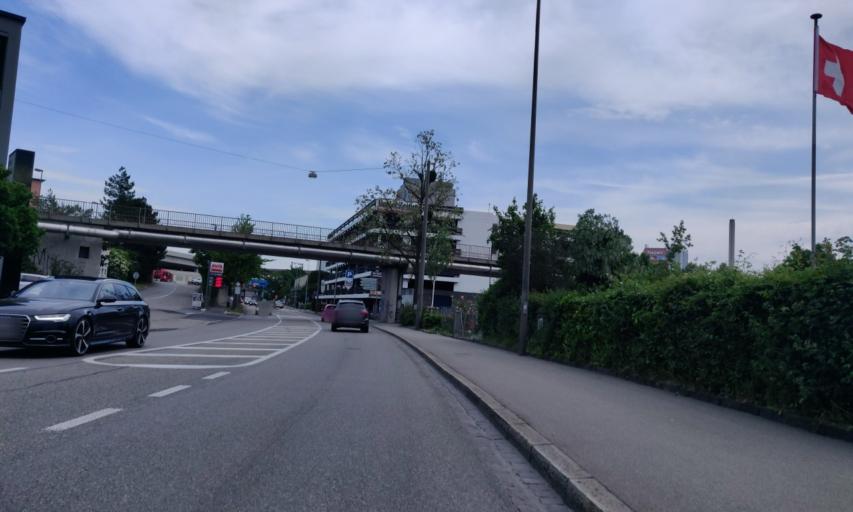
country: FR
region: Alsace
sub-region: Departement du Haut-Rhin
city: Village-Neuf
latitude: 47.5774
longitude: 7.5963
